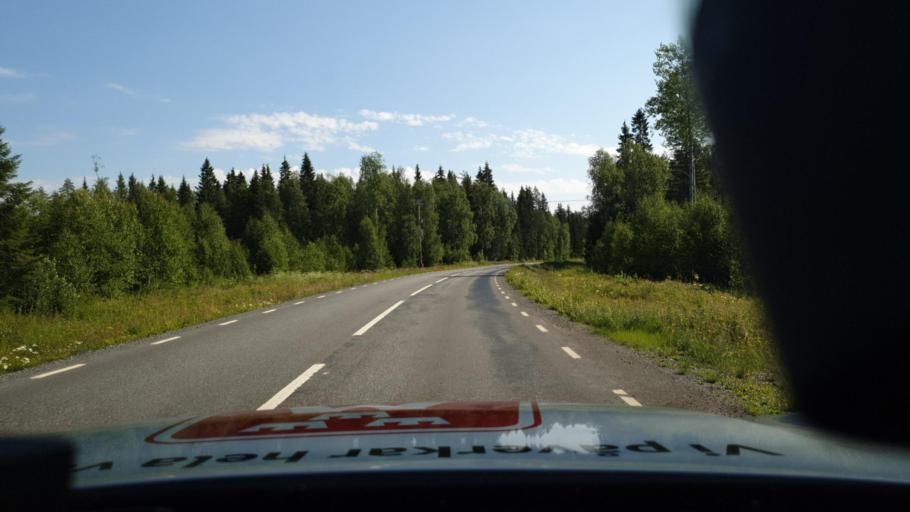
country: SE
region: Norrbotten
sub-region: Lulea Kommun
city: Gammelstad
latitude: 65.7899
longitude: 22.1170
